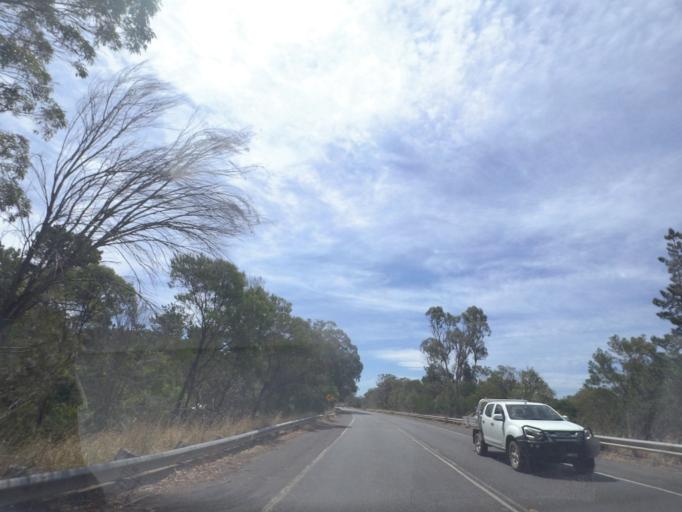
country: AU
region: New South Wales
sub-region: Wollondilly
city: Buxton
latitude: -34.2708
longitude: 150.5751
